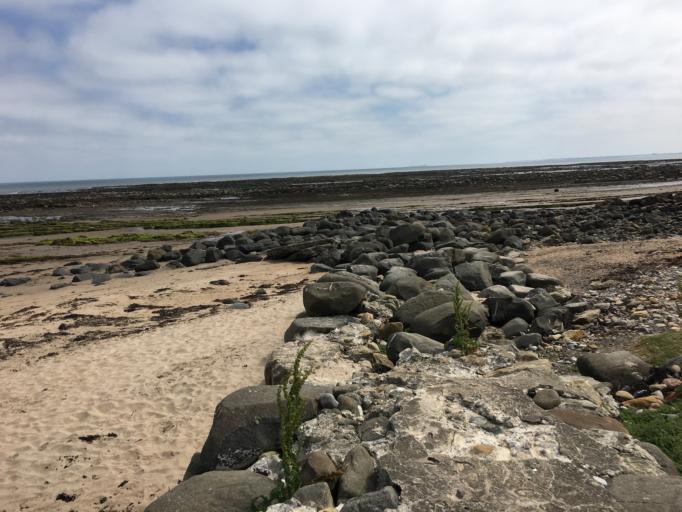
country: GB
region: England
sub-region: Northumberland
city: Alnmouth
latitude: 55.3986
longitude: -1.5945
